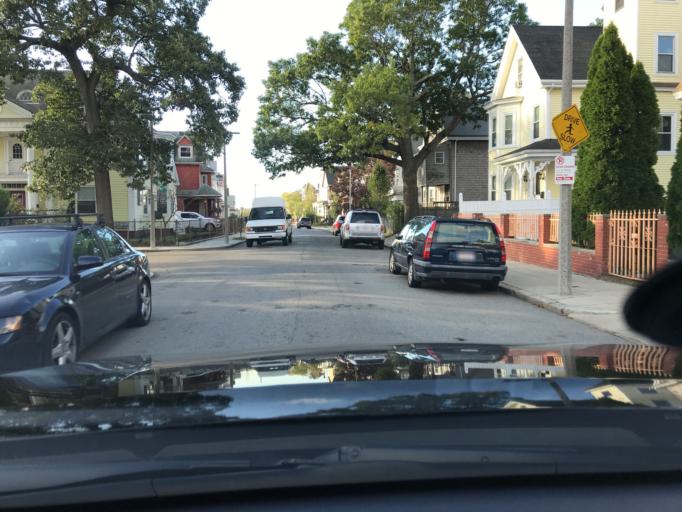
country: US
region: Massachusetts
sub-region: Suffolk County
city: South Boston
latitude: 42.3163
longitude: -71.0729
